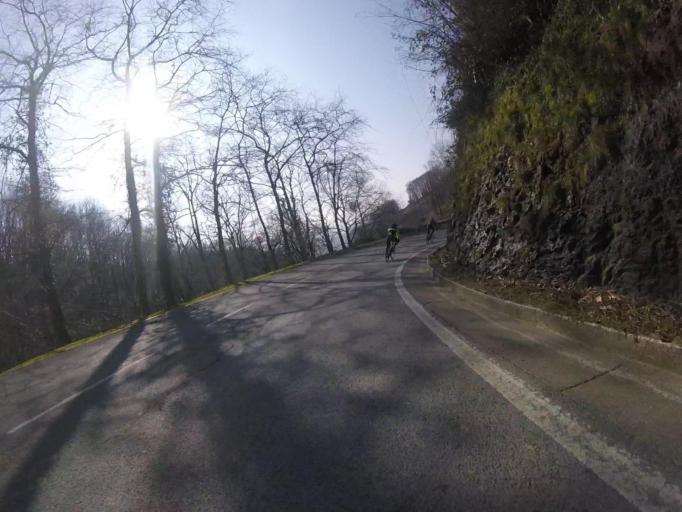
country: ES
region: Navarre
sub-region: Provincia de Navarra
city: Bera
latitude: 43.3083
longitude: -1.6892
